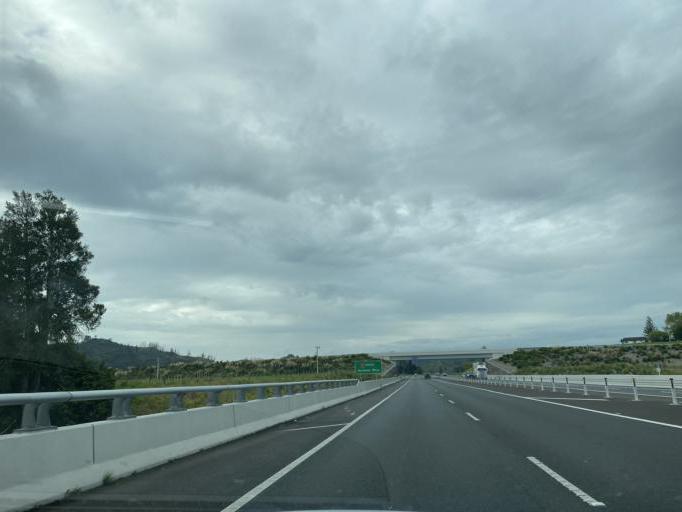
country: NZ
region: Waikato
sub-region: Waikato District
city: Ngaruawahia
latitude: -37.6139
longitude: 175.2047
